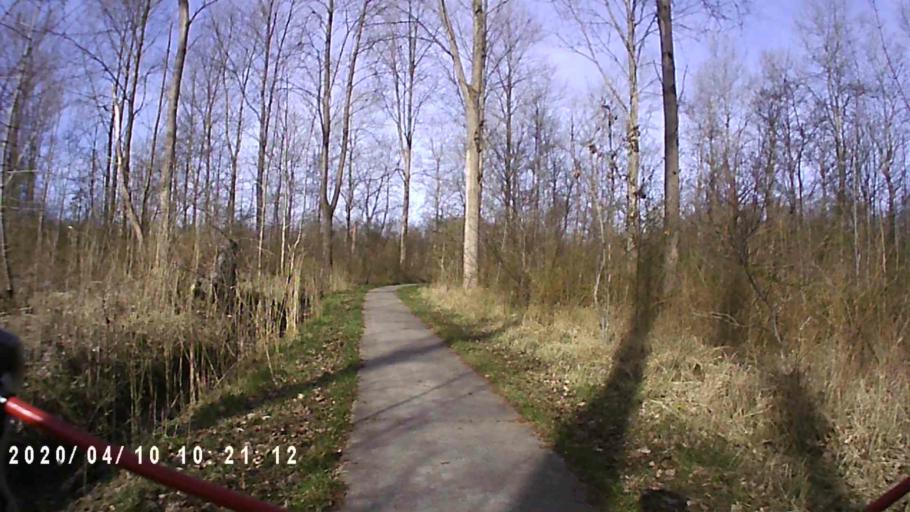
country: NL
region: Friesland
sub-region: Gemeente Dongeradeel
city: Anjum
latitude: 53.3807
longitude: 6.2189
